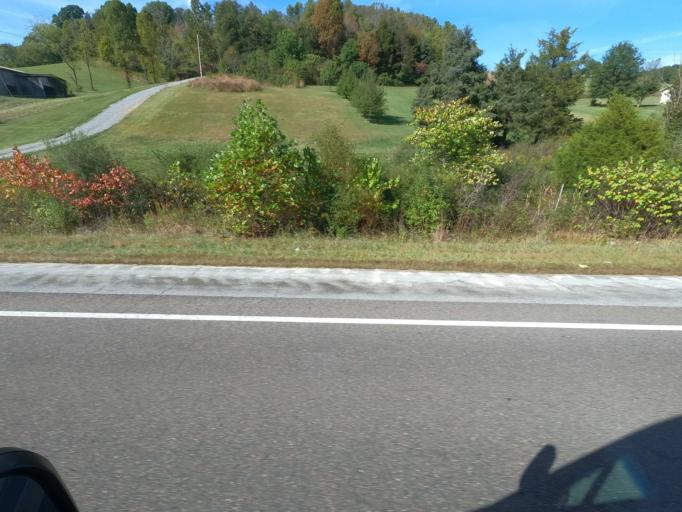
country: US
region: Tennessee
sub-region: Sullivan County
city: Blountville
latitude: 36.5788
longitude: -82.3086
